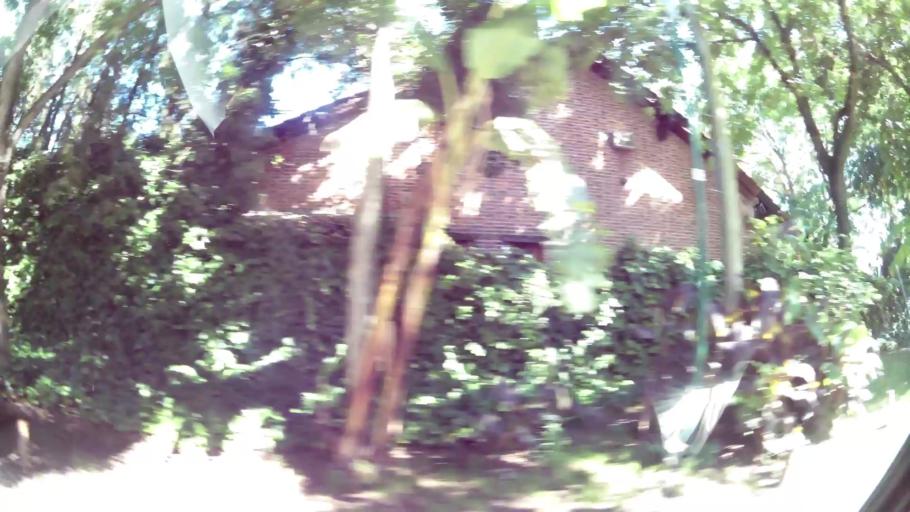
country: AR
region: Buenos Aires
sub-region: Partido de Tigre
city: Tigre
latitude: -34.4833
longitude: -58.5748
